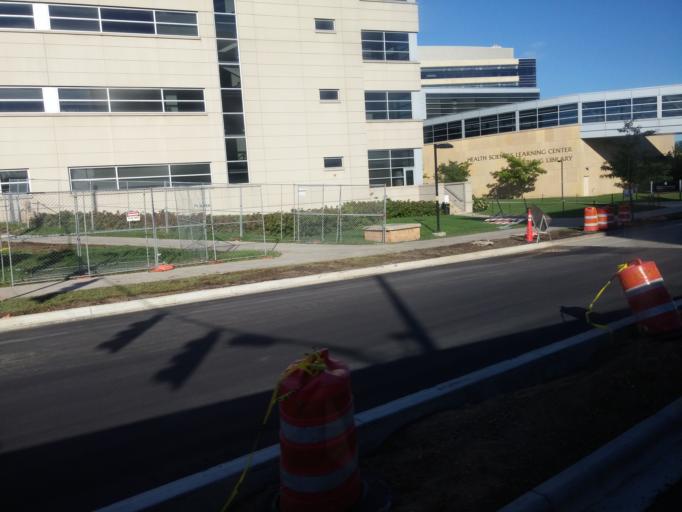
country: US
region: Wisconsin
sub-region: Dane County
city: Shorewood Hills
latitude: 43.0772
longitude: -89.4290
